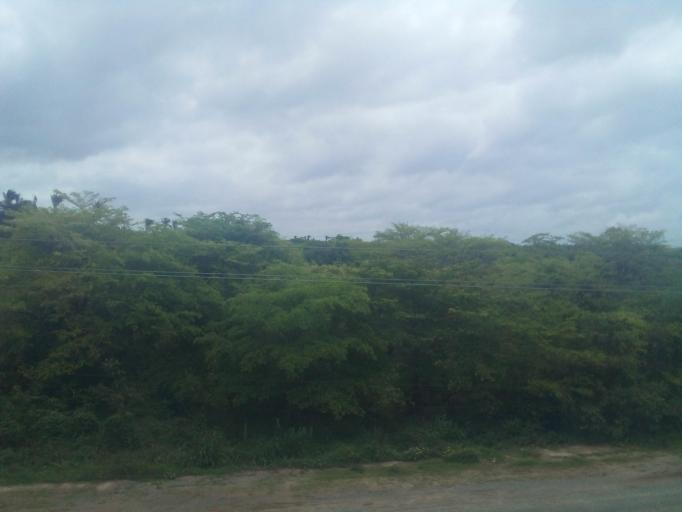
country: BR
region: Maranhao
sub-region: Arari
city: Arari
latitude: -3.5754
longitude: -44.7418
